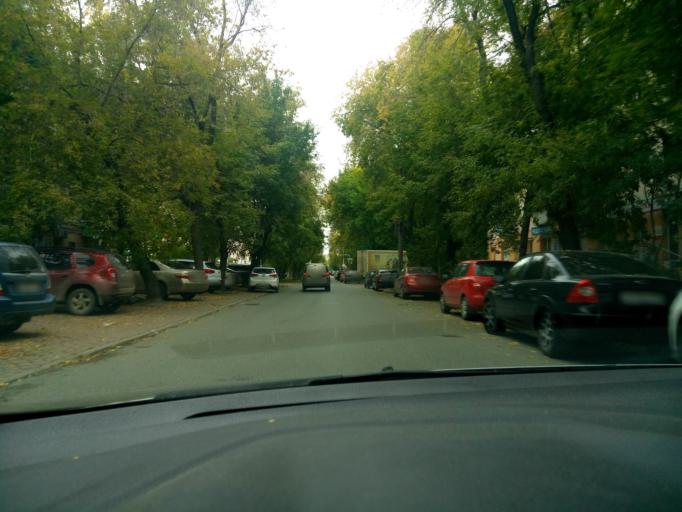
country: RU
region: Sverdlovsk
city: Yekaterinburg
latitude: 56.8373
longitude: 60.6274
